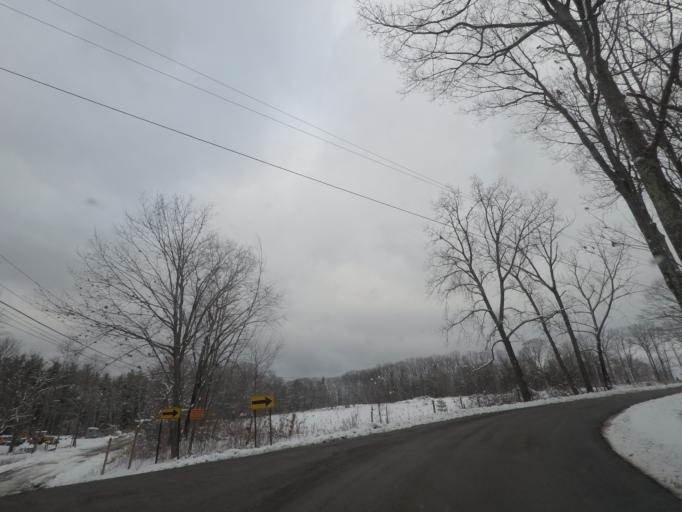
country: US
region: New York
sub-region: Rensselaer County
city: Averill Park
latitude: 42.6636
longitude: -73.5331
